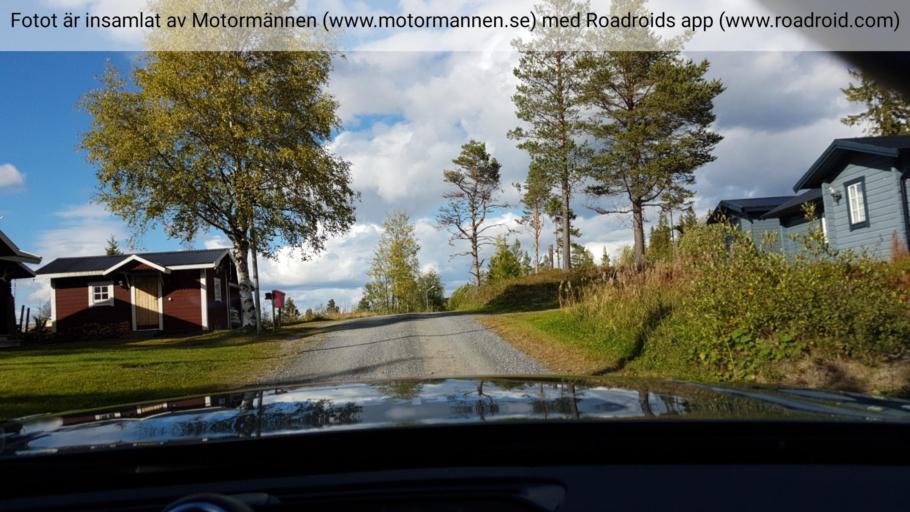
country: SE
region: Jaemtland
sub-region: Are Kommun
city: Jarpen
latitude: 63.2311
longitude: 13.6774
